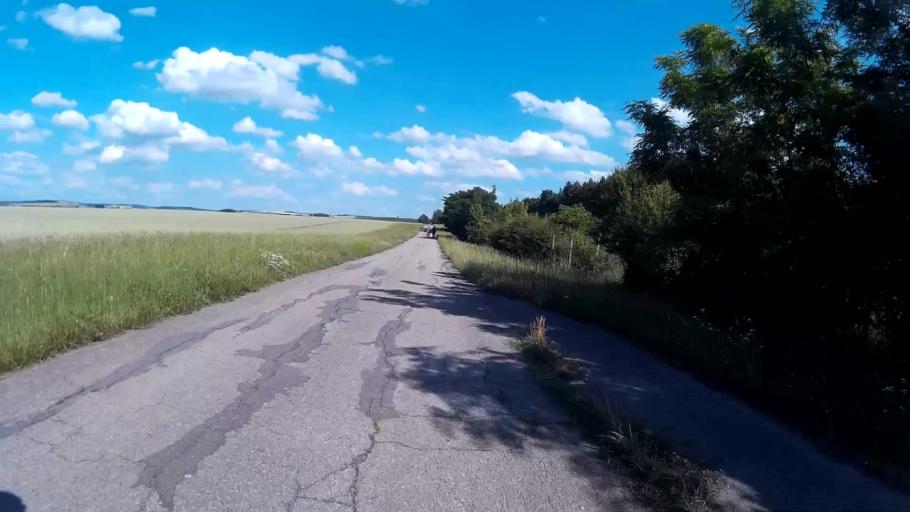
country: CZ
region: South Moravian
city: Moutnice
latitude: 49.0452
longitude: 16.7033
